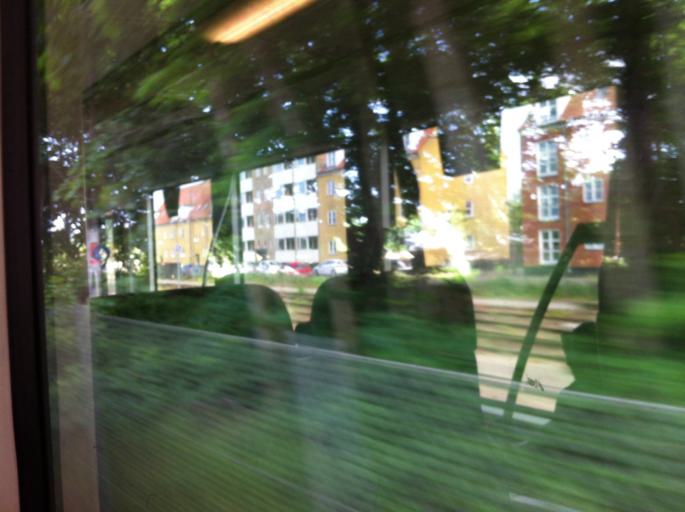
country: DK
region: Capital Region
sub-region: Helsingor Kommune
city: Helsingor
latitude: 56.0404
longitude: 12.6104
